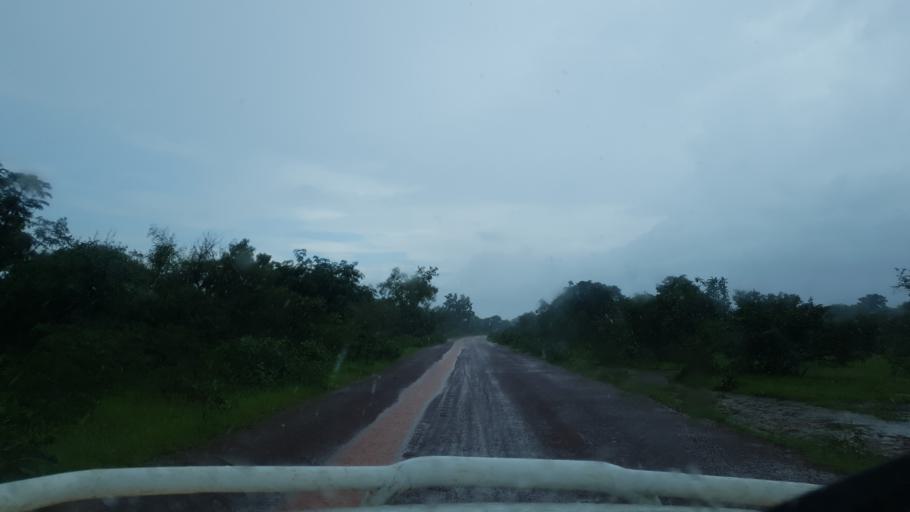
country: ML
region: Sikasso
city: Kolondieba
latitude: 11.6031
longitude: -6.6727
